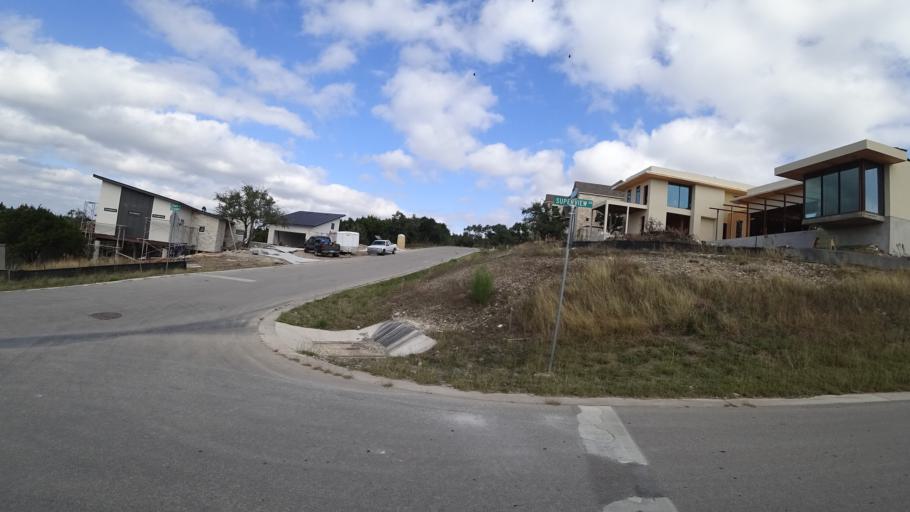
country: US
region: Texas
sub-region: Travis County
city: Bee Cave
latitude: 30.2534
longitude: -97.9268
